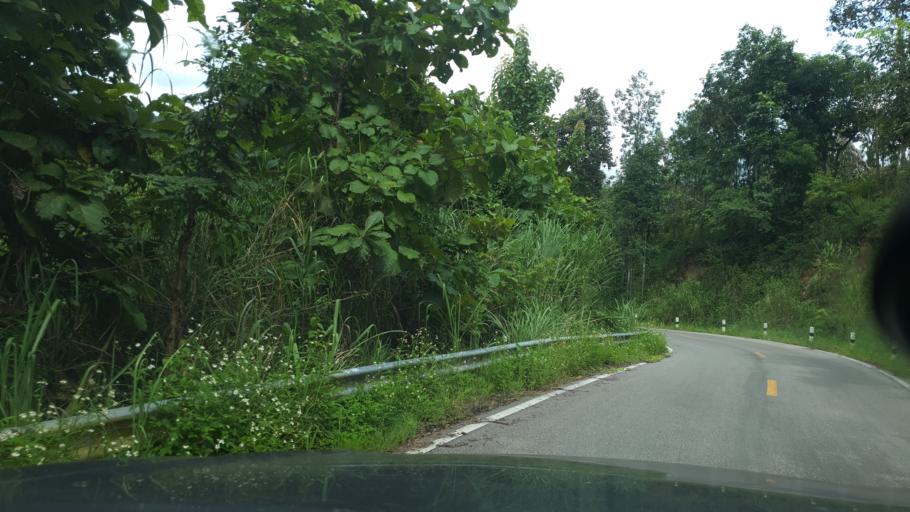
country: TH
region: Lamphun
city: Mae Tha
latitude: 18.5191
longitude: 99.2624
